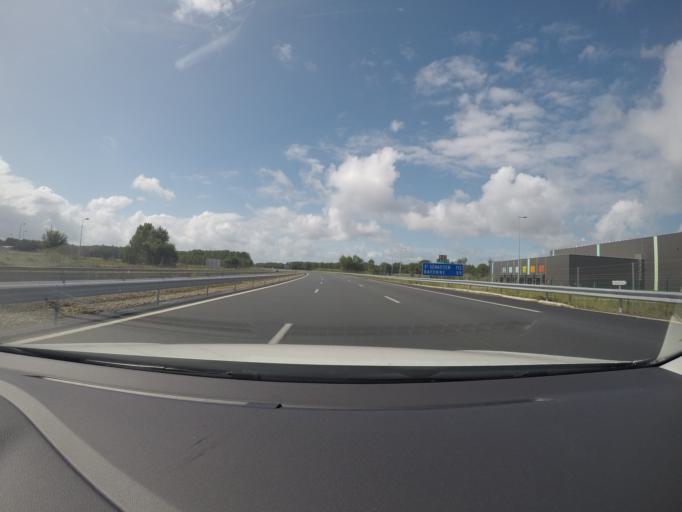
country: FR
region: Aquitaine
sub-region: Departement des Landes
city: Castets
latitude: 43.8692
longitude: -1.1516
